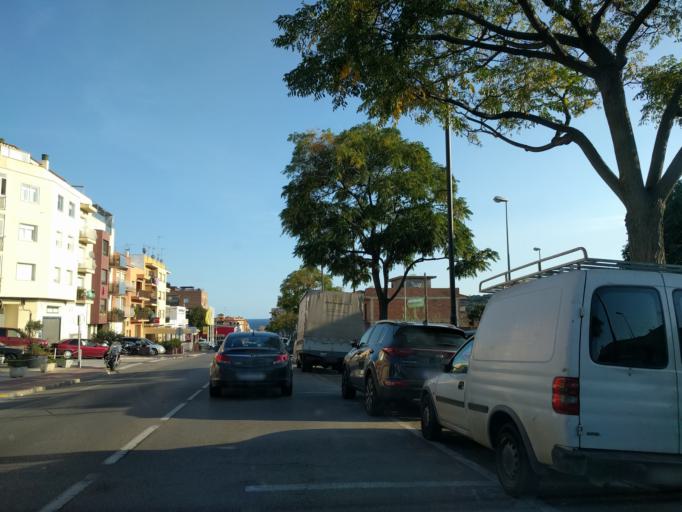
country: ES
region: Catalonia
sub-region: Provincia de Girona
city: Sant Feliu de Guixols
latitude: 41.7899
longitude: 3.0224
